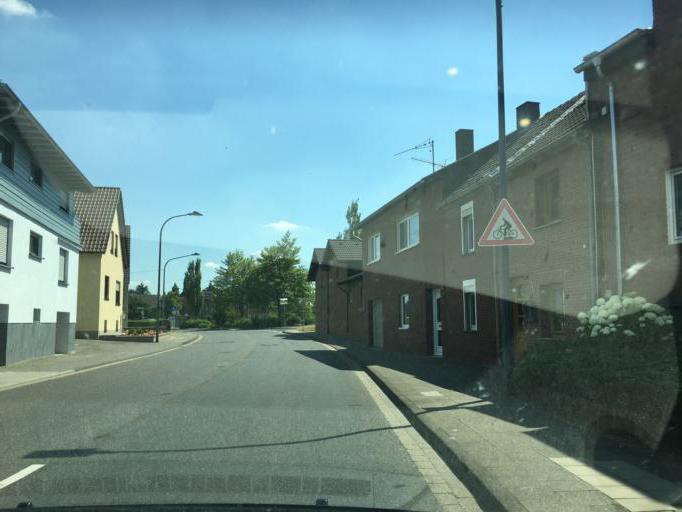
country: DE
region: North Rhine-Westphalia
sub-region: Regierungsbezirk Koln
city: Langerwehe
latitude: 50.8106
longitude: 6.3751
